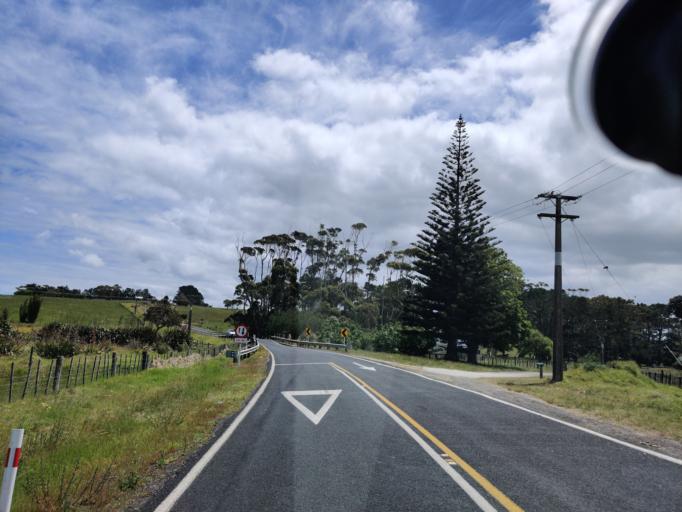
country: NZ
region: Northland
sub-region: Far North District
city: Kaitaia
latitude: -34.7086
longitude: 173.0344
